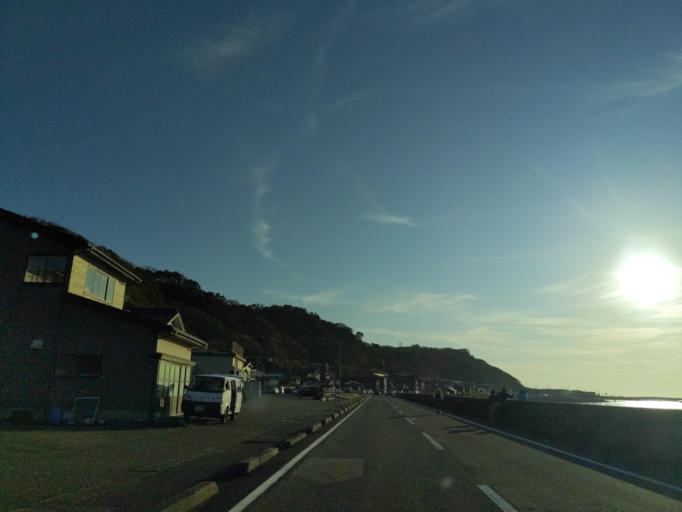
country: JP
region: Niigata
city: Nagaoka
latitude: 37.5484
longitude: 138.6965
